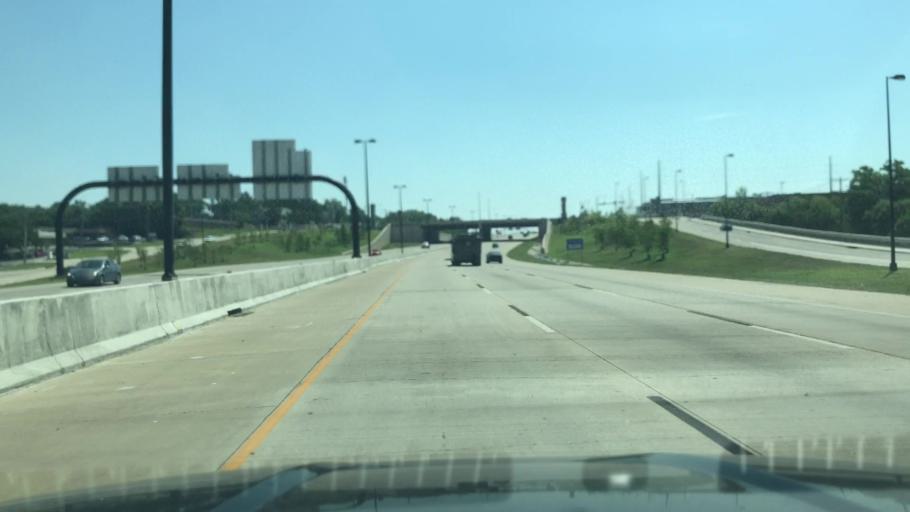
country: US
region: Oklahoma
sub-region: Tulsa County
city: Jenks
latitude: 36.0901
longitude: -95.9620
